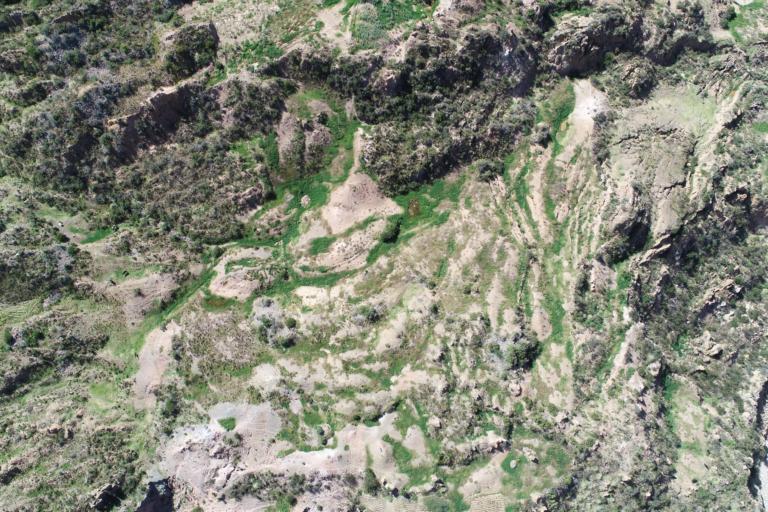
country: BO
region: La Paz
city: La Paz
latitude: -16.5592
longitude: -67.9872
